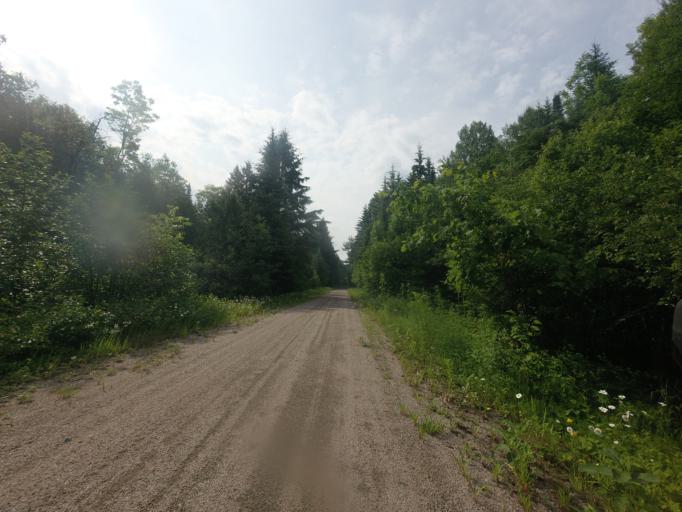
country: CA
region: Quebec
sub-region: Outaouais
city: Maniwaki
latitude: 46.2770
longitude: -76.0141
